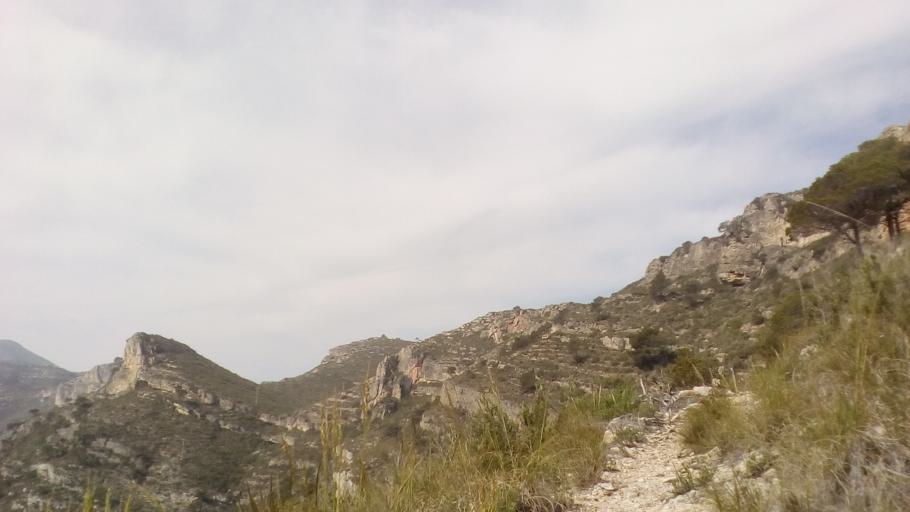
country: ES
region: Valencia
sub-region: Provincia de Valencia
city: Xeraco,Jaraco
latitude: 39.0383
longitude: -0.2381
